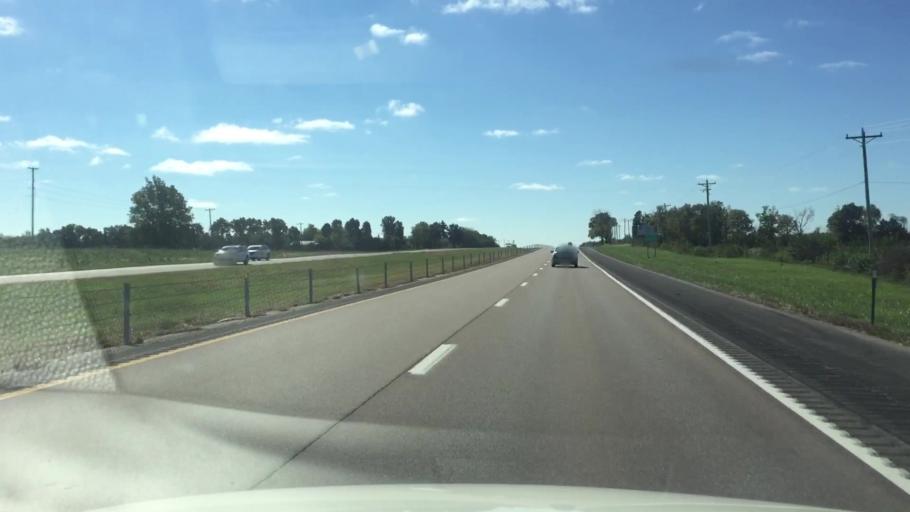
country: US
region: Missouri
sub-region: Boone County
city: Ashland
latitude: 38.7882
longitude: -92.2523
